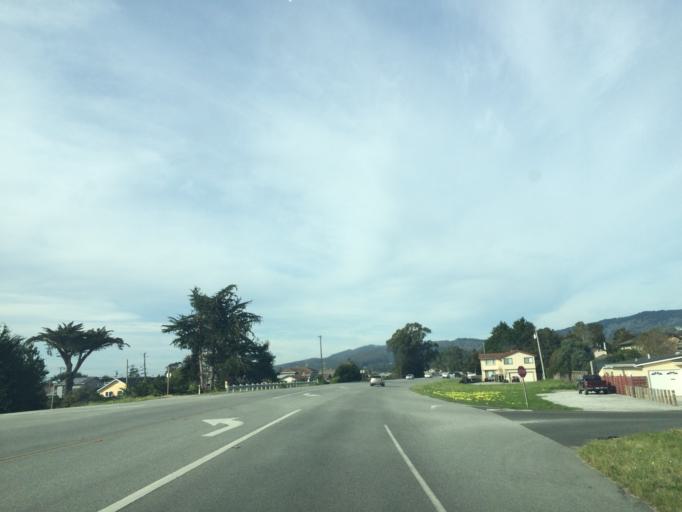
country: US
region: California
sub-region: San Mateo County
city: Half Moon Bay
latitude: 37.4582
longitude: -122.4340
